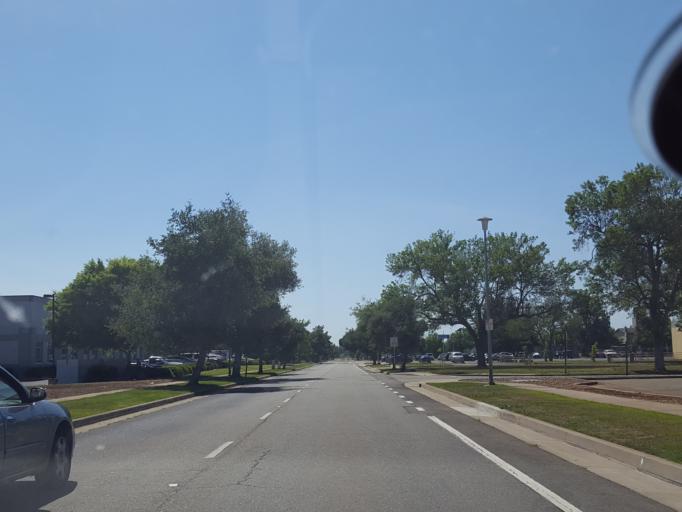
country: US
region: California
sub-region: Sacramento County
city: Rancho Cordova
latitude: 38.5669
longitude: -121.2940
